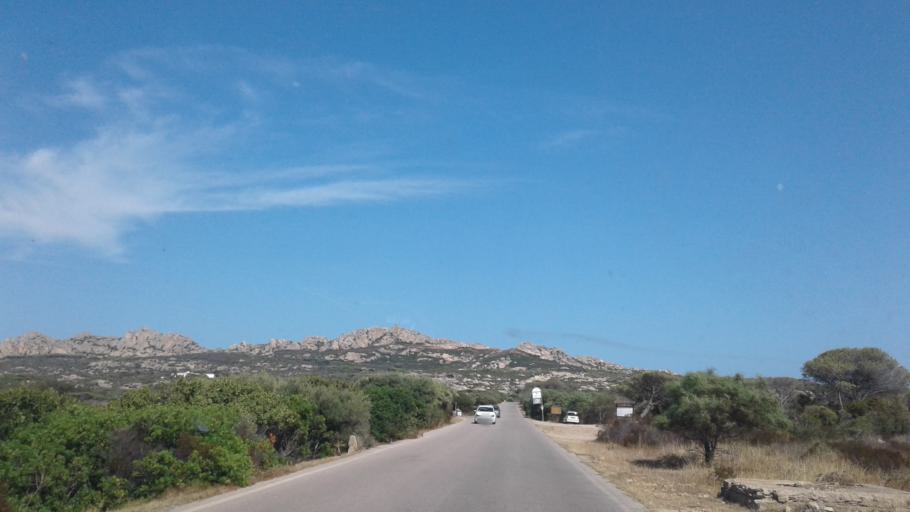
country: IT
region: Sardinia
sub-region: Provincia di Olbia-Tempio
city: La Maddalena
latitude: 41.2150
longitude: 9.4490
